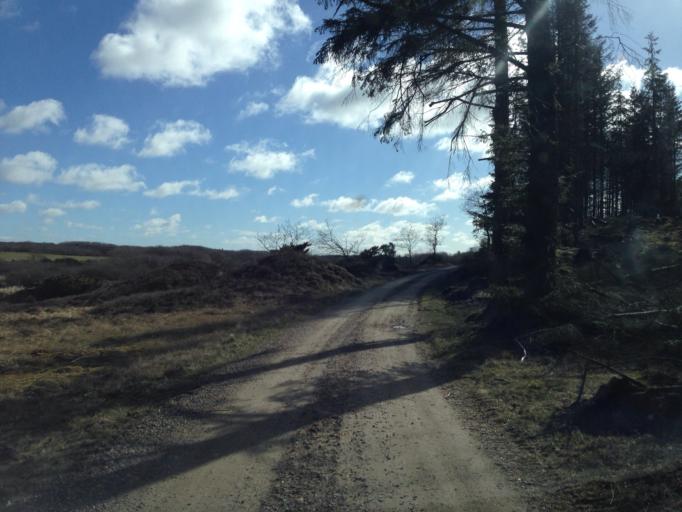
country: DK
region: Central Jutland
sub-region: Holstebro Kommune
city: Holstebro
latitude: 56.2552
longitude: 8.5012
